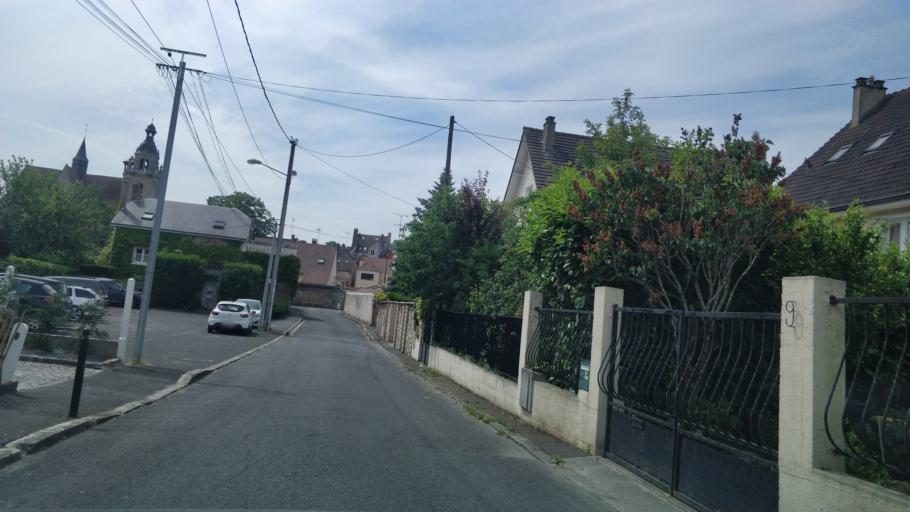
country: FR
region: Ile-de-France
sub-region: Departement de l'Essonne
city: Limours
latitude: 48.6475
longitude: 2.0769
